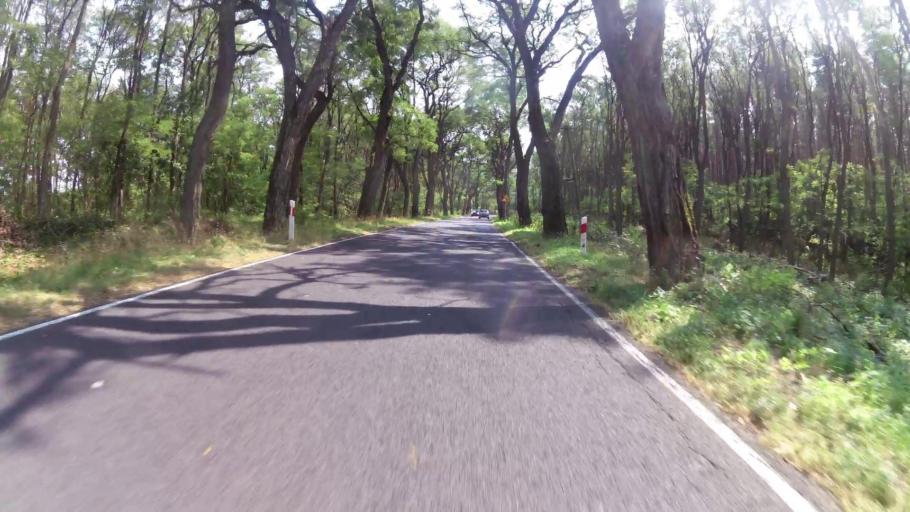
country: PL
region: West Pomeranian Voivodeship
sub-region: Powiat gryfinski
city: Moryn
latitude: 52.8338
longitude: 14.4136
